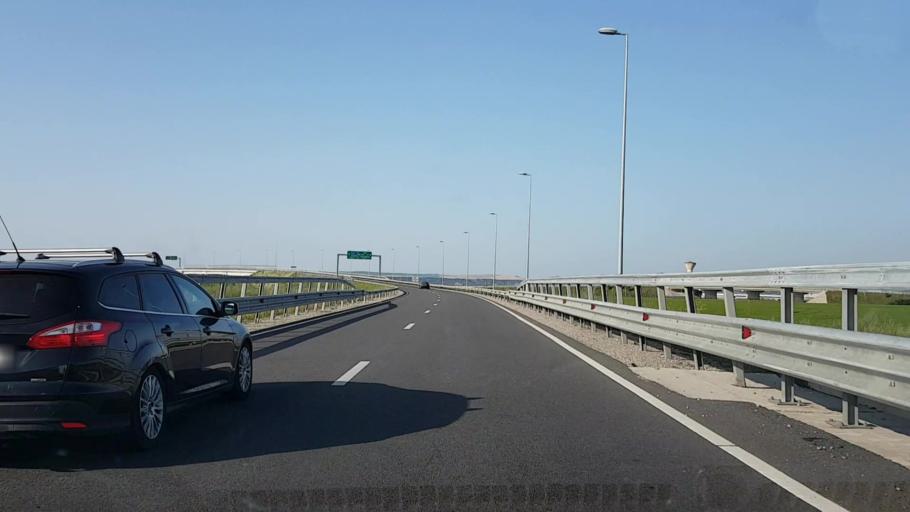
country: RO
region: Cluj
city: Turda
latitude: 46.5210
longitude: 23.7991
